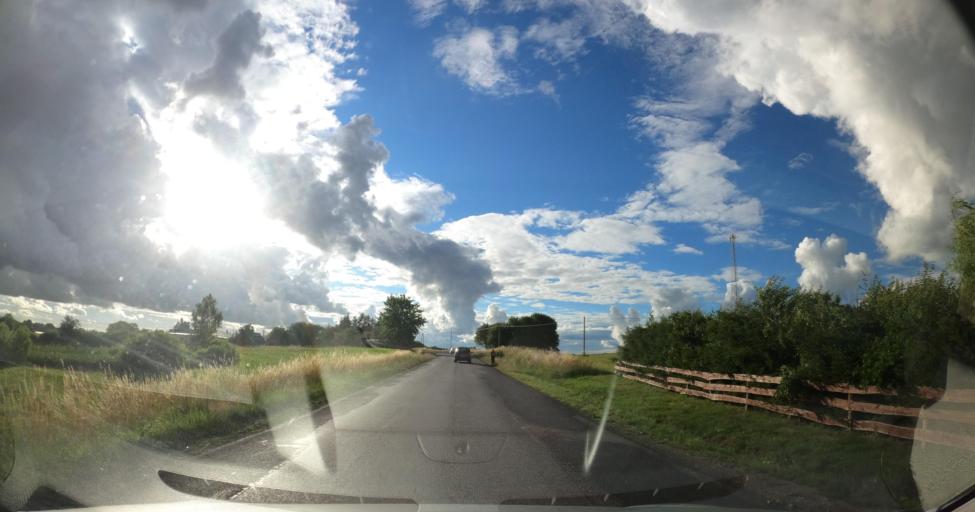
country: PL
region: Pomeranian Voivodeship
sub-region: Powiat bytowski
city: Czarna Dabrowka
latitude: 54.3531
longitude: 17.5753
